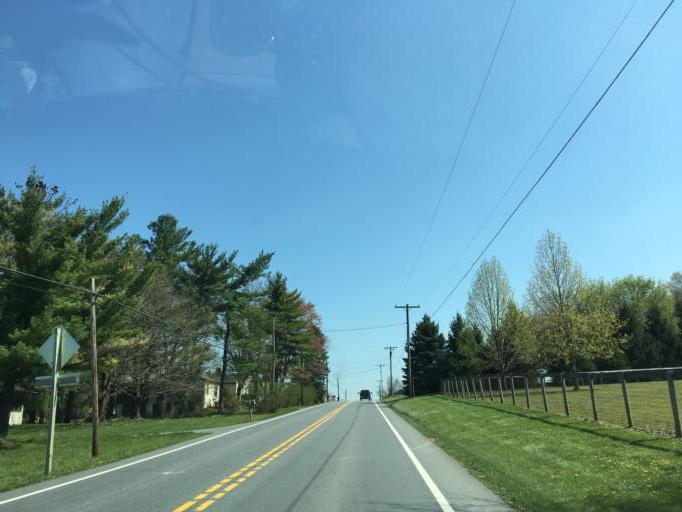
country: US
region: Maryland
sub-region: Frederick County
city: Woodsboro
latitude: 39.5198
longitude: -77.2925
